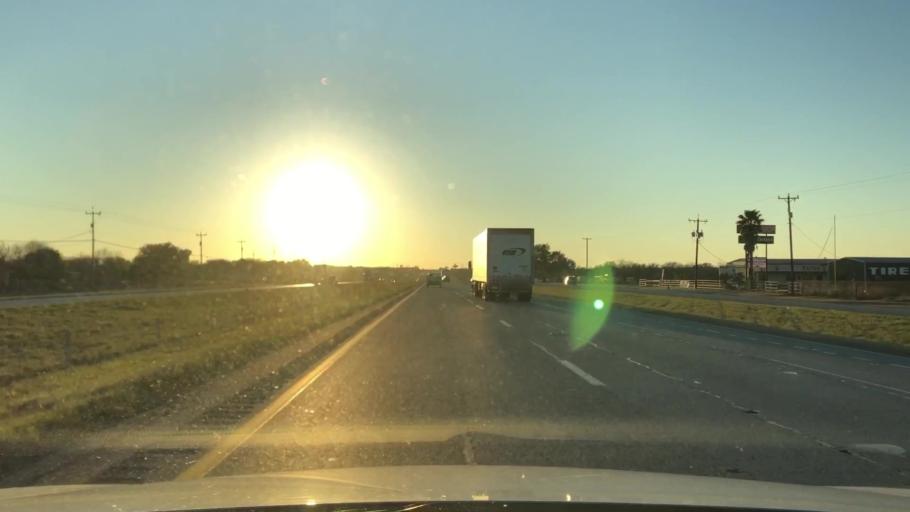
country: US
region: Texas
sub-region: Guadalupe County
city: Cibolo
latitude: 29.4969
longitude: -98.1983
